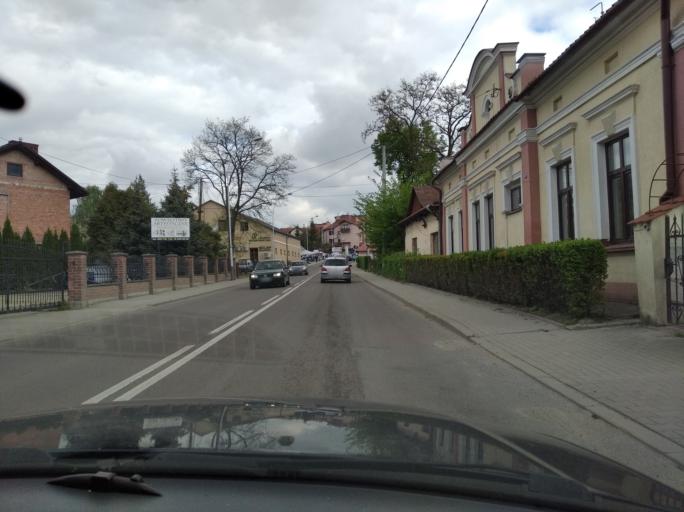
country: PL
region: Subcarpathian Voivodeship
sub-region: Powiat przeworski
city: Przeworsk
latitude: 50.0546
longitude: 22.4923
